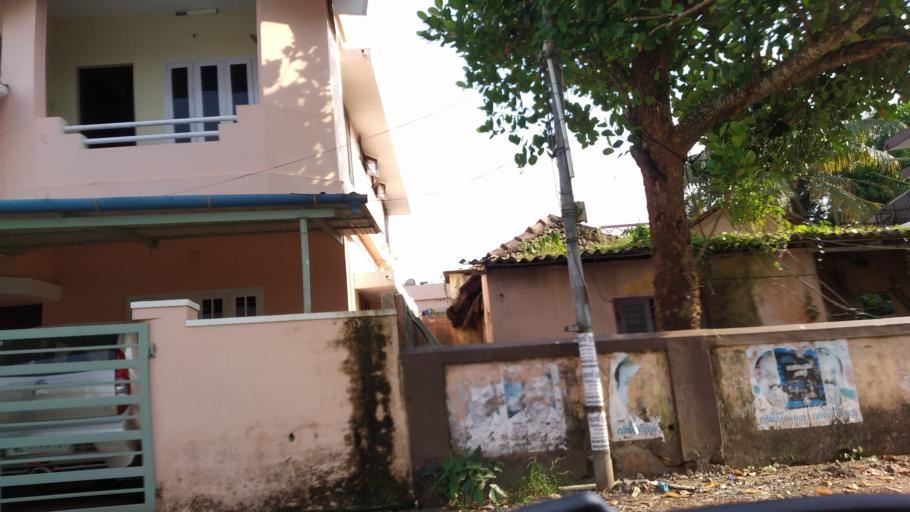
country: IN
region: Kerala
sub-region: Ernakulam
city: Elur
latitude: 10.0010
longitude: 76.2843
